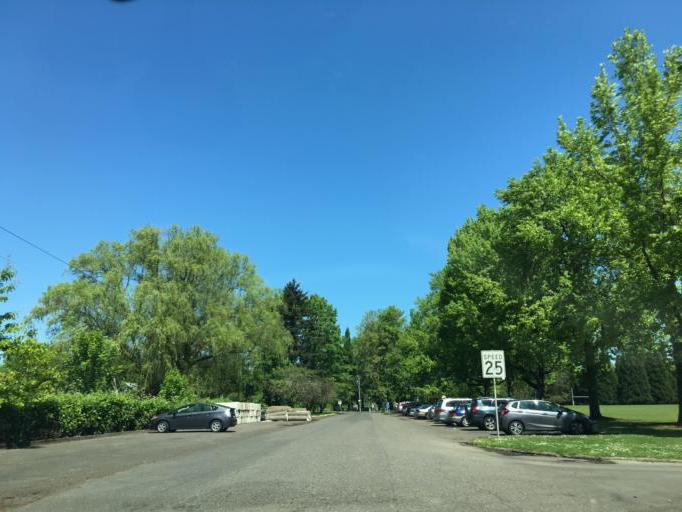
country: US
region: Oregon
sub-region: Clackamas County
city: Milwaukie
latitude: 45.4670
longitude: -122.6415
